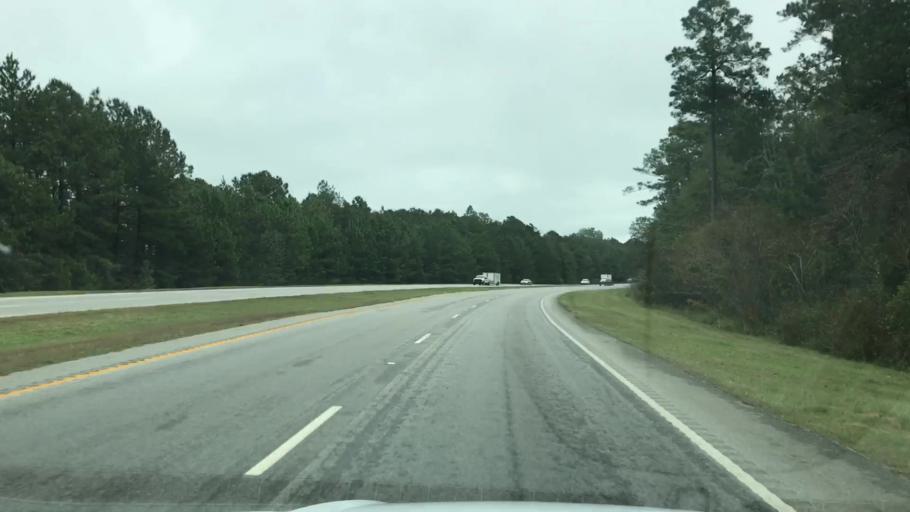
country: US
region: South Carolina
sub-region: Beaufort County
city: Bluffton
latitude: 32.3540
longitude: -80.9108
